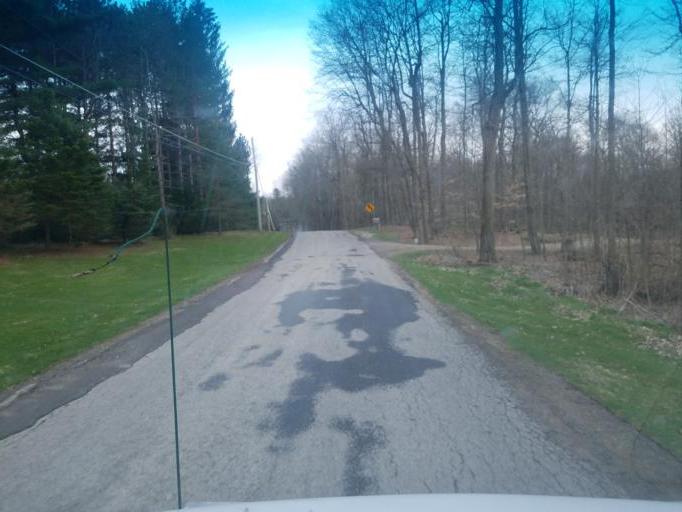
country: US
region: Ohio
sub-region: Richland County
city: Ontario
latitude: 40.7325
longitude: -82.6049
